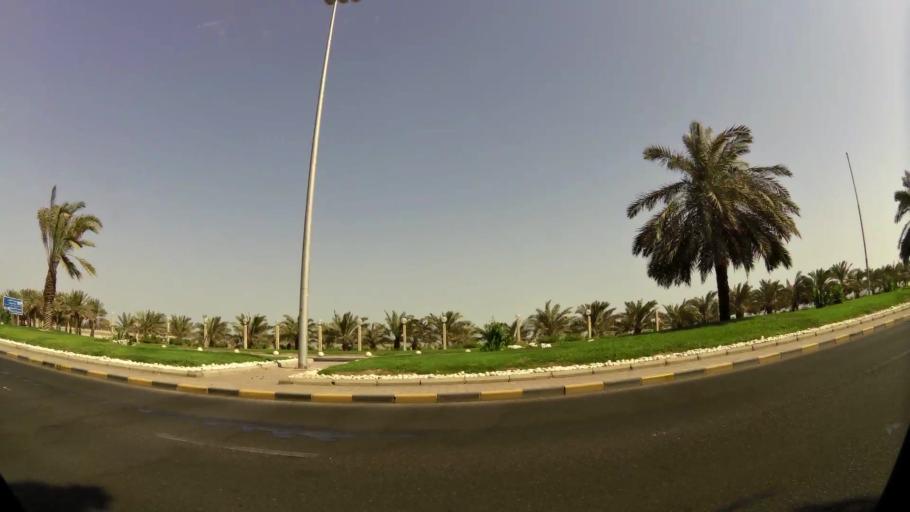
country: KW
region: Muhafazat Hawalli
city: Hawalli
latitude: 29.3573
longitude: 48.0264
